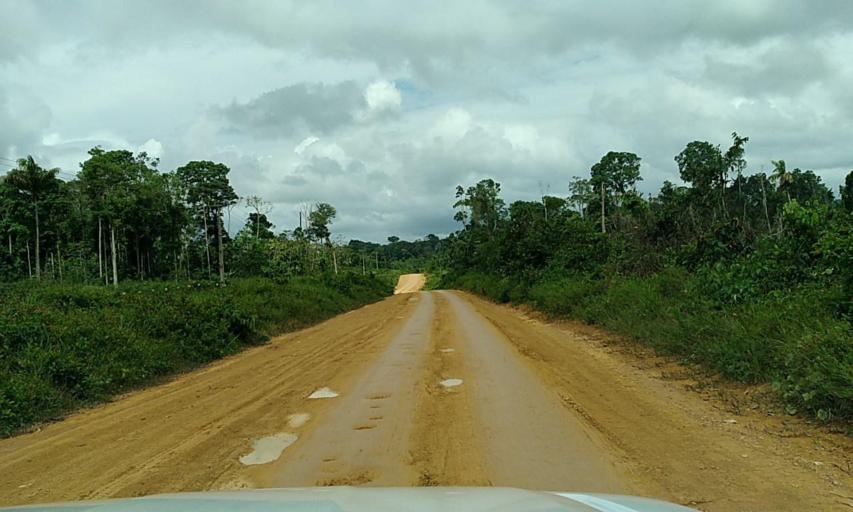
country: BR
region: Para
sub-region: Senador Jose Porfirio
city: Senador Jose Porfirio
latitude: -2.7597
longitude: -51.7905
